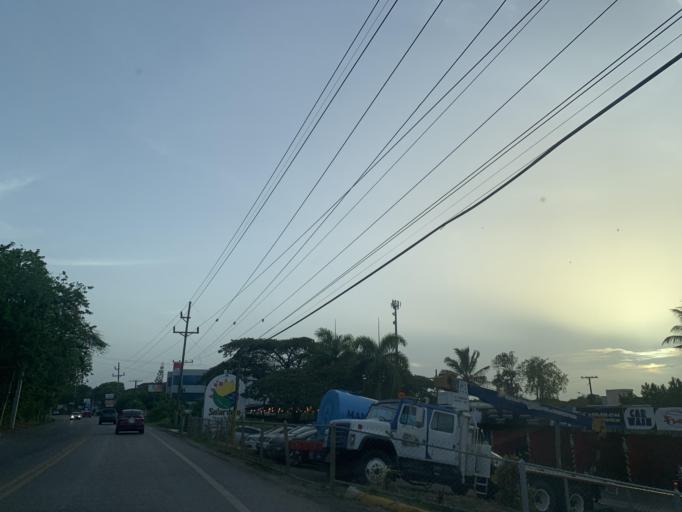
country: DO
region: Puerto Plata
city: Cabarete
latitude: 19.7698
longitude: -70.5036
